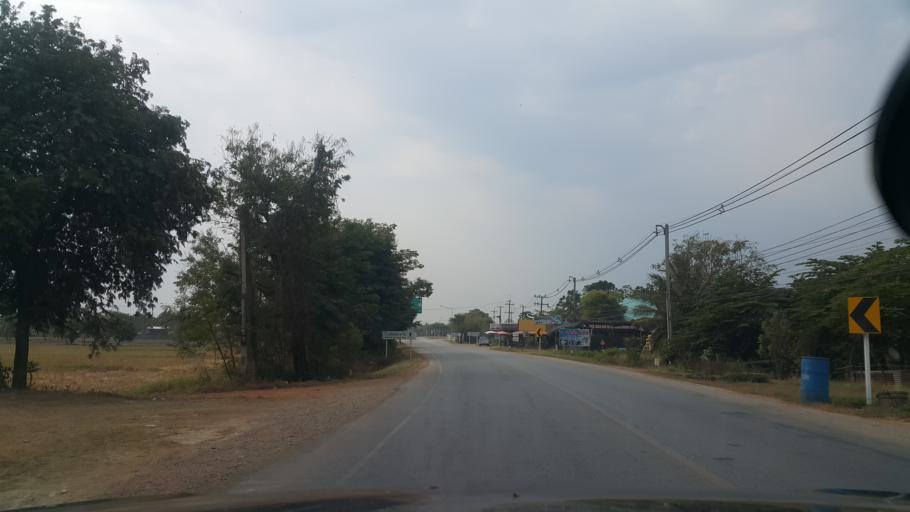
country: TH
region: Sukhothai
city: Sukhothai
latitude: 17.0670
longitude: 99.8780
